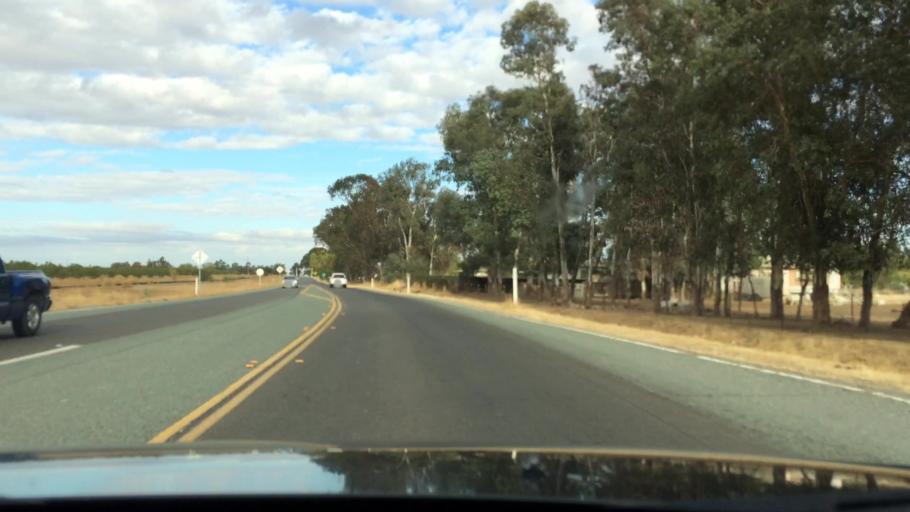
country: US
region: California
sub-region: Sacramento County
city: Herald
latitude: 38.2922
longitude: -121.2507
